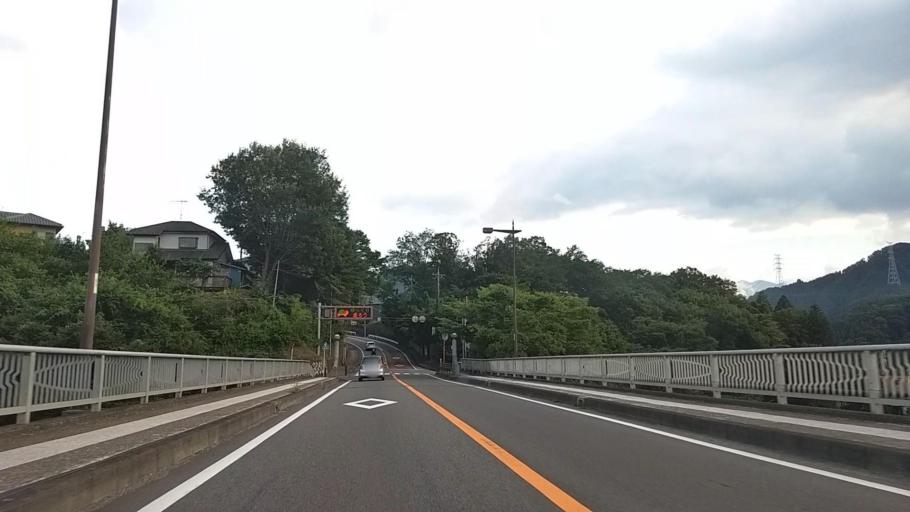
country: JP
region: Yamanashi
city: Uenohara
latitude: 35.5935
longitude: 139.2260
